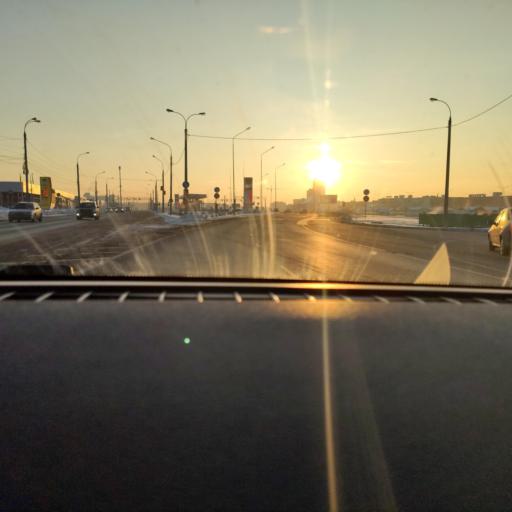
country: RU
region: Samara
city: Samara
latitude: 53.1417
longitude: 50.1816
